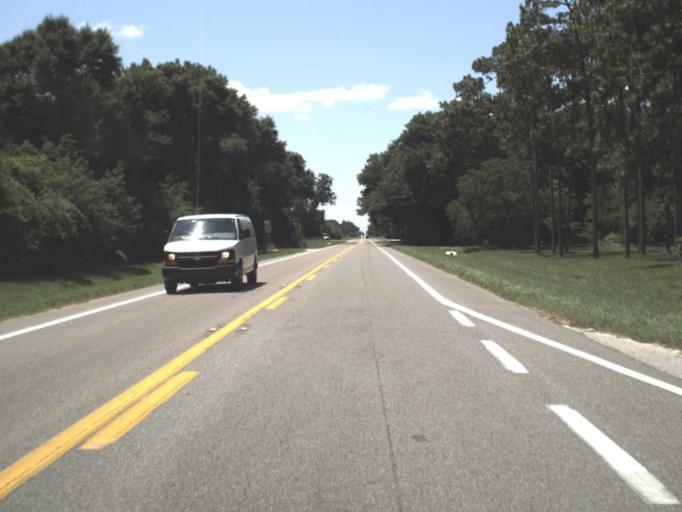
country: US
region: Florida
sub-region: Lafayette County
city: Mayo
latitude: 29.9819
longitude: -82.9962
